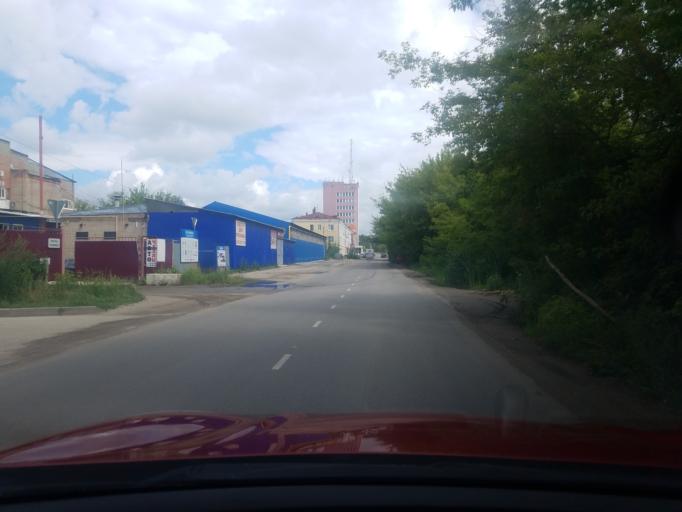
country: RU
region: Orjol
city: Znamenka
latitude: 52.9185
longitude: 35.9893
